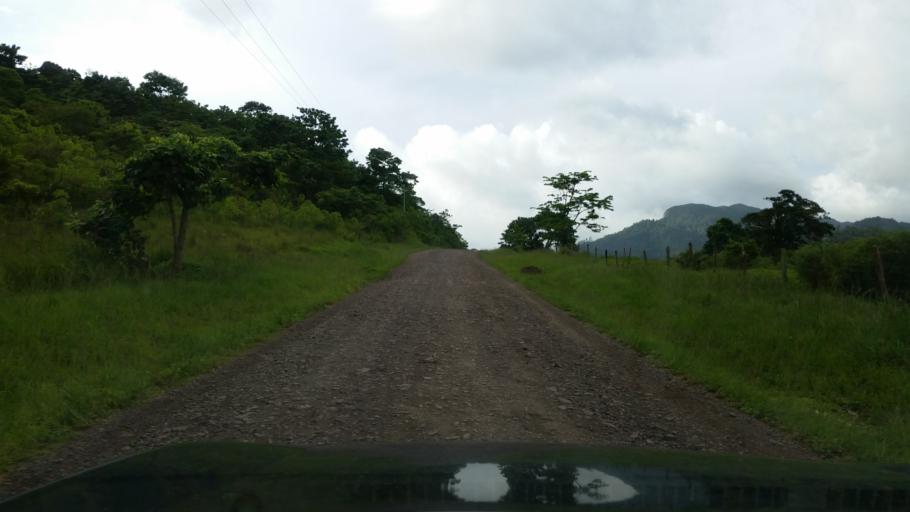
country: NI
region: Jinotega
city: Jinotega
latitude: 13.2250
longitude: -85.7303
